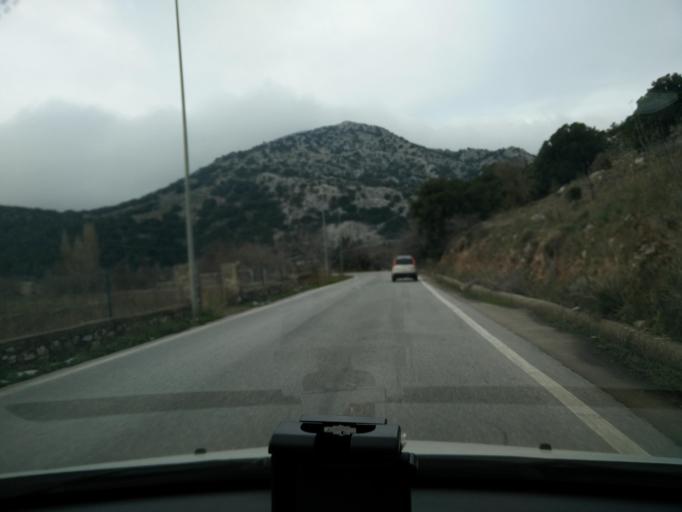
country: GR
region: Crete
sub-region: Nomos Irakleiou
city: Malia
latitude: 35.2022
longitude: 25.4795
